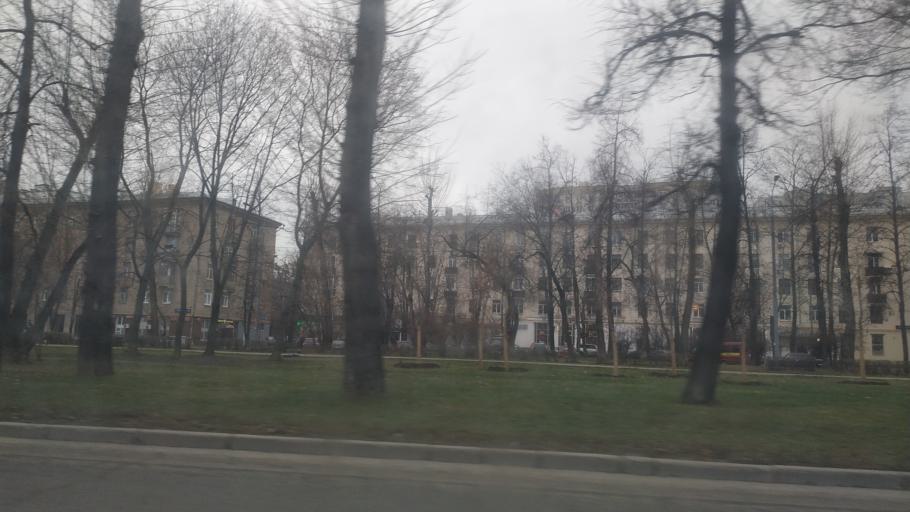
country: RU
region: Moskovskaya
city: Vostochnoe Degunino
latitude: 55.8836
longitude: 37.5430
